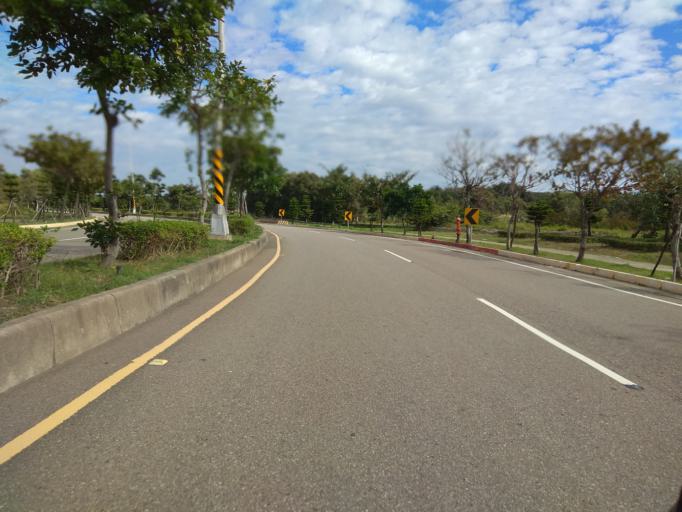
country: TW
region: Taiwan
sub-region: Hsinchu
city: Zhubei
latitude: 25.0349
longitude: 121.0717
